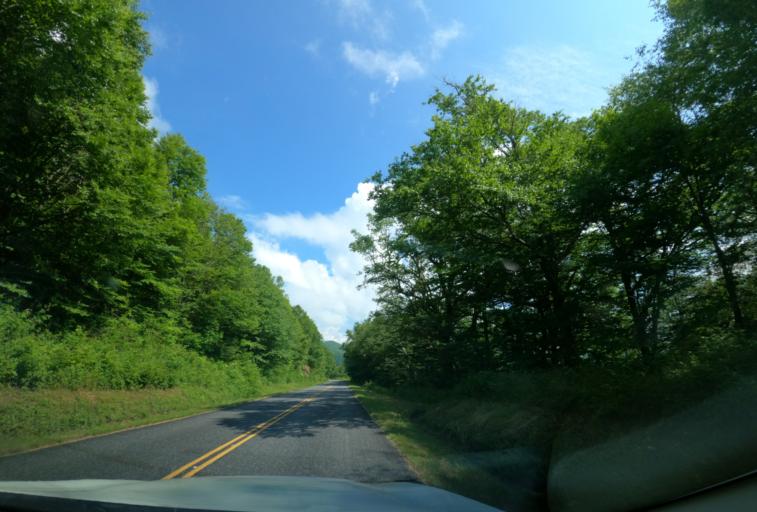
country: US
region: North Carolina
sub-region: Haywood County
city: Hazelwood
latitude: 35.3931
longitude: -83.0379
